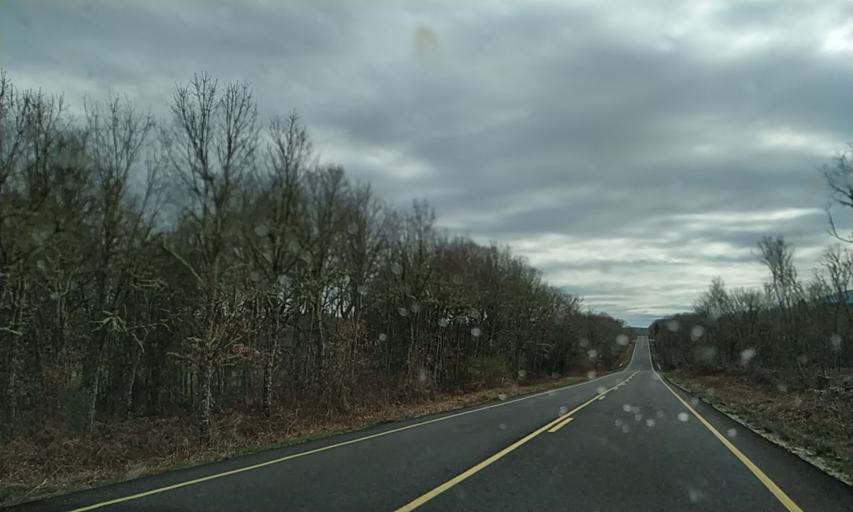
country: ES
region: Castille and Leon
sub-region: Provincia de Salamanca
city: Penaparda
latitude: 40.2903
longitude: -6.6660
